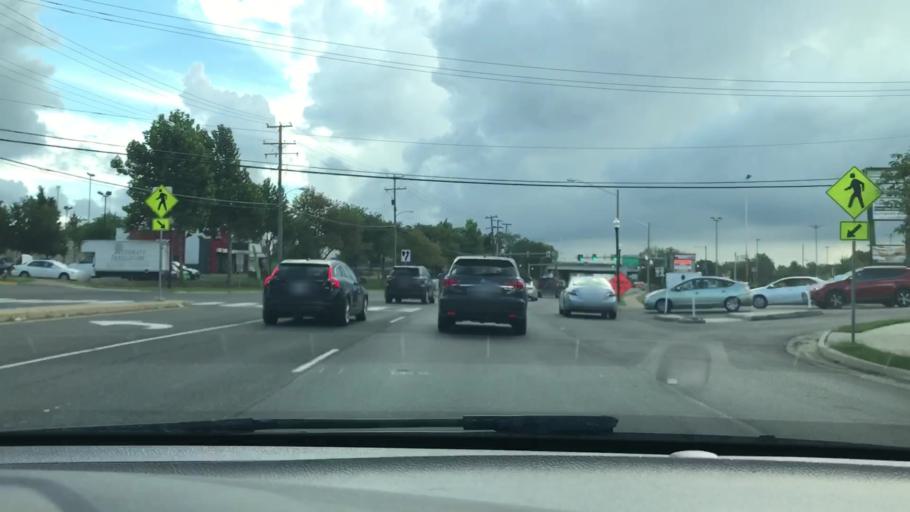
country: US
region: Virginia
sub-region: Fairfax County
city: Baileys Crossroads
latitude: 38.8521
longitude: -77.1257
